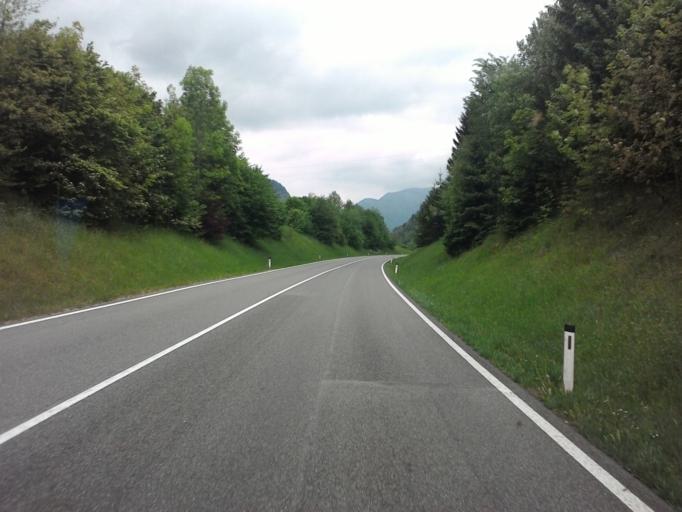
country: AT
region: Styria
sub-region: Politischer Bezirk Liezen
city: Altenmarkt bei Sankt Gallen
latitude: 47.7486
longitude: 14.6432
